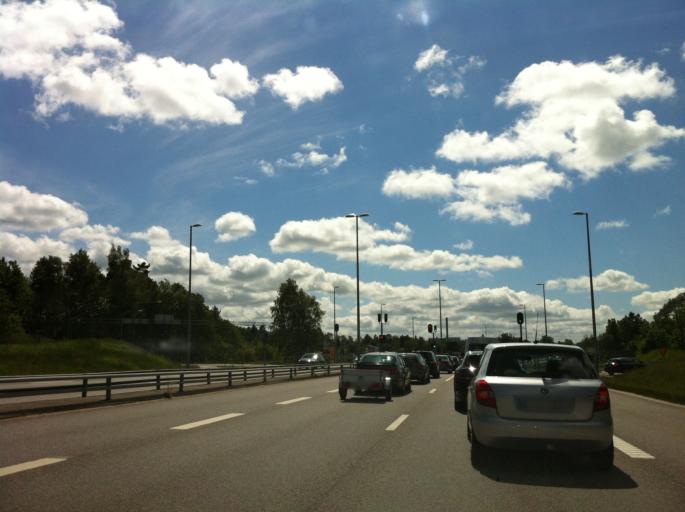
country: SE
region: Vaestra Goetaland
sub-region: Trollhattan
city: Trollhattan
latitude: 58.2638
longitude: 12.2920
